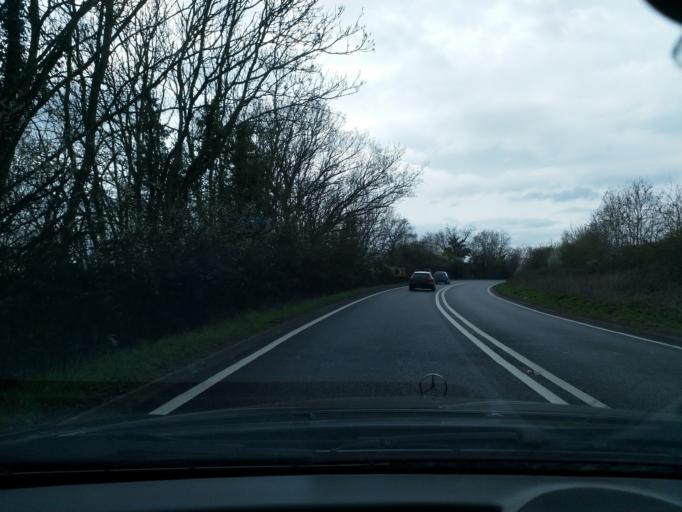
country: GB
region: England
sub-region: Warwickshire
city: Stratford-upon-Avon
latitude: 52.2225
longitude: -1.6666
